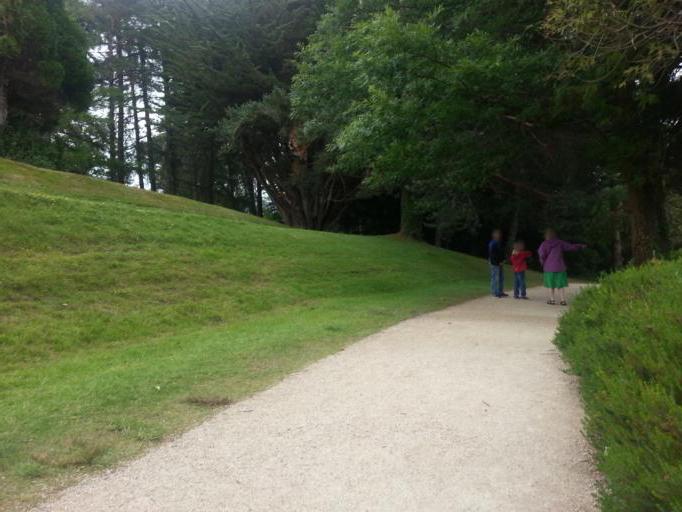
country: IE
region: Leinster
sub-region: Wicklow
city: Enniskerry
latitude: 53.1838
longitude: -6.1840
